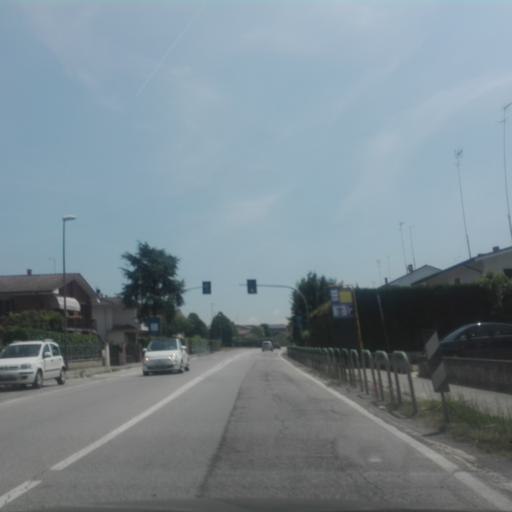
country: IT
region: Veneto
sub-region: Provincia di Rovigo
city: Adria
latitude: 45.0575
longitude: 12.0629
